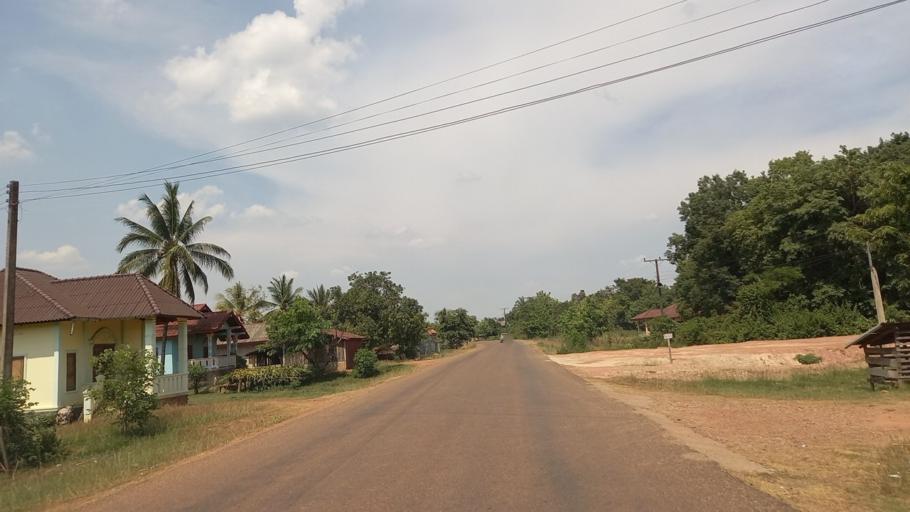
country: LA
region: Bolikhamxai
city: Muang Pakxan
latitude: 18.4044
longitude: 103.6937
